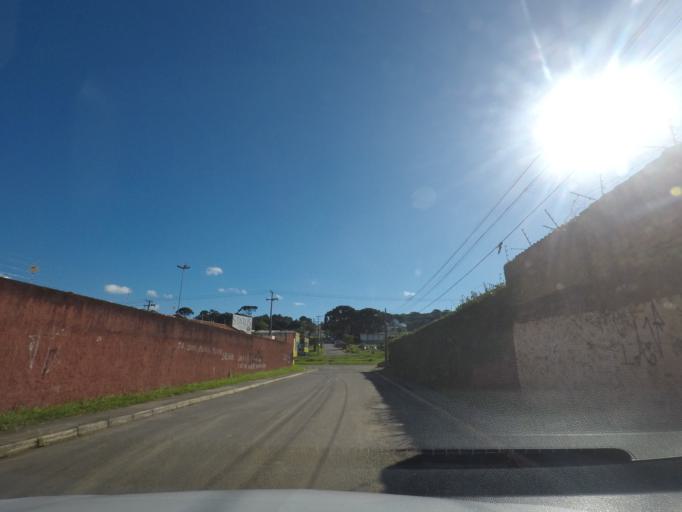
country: BR
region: Parana
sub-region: Almirante Tamandare
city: Almirante Tamandare
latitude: -25.3434
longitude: -49.2825
